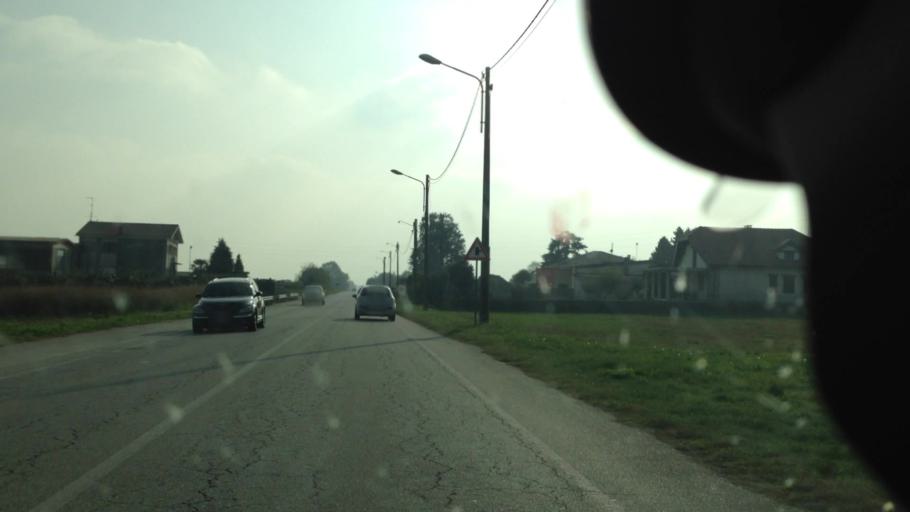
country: IT
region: Piedmont
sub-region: Provincia di Vercelli
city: Borgo d'Ale
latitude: 45.3405
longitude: 8.0462
